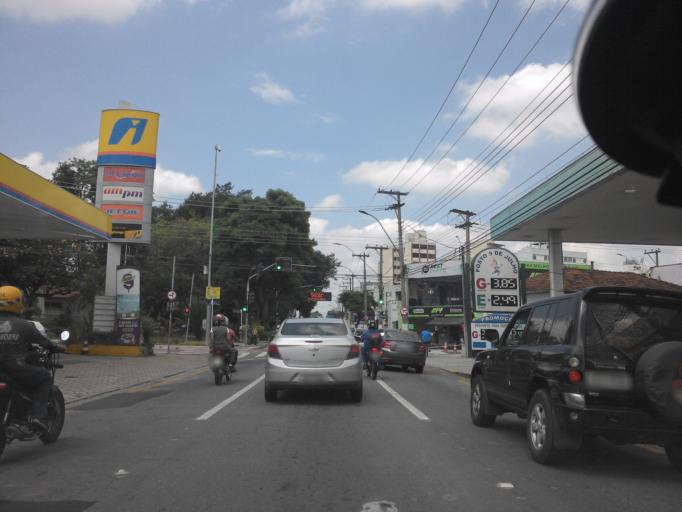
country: BR
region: Sao Paulo
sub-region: Taubate
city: Taubate
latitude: -23.0240
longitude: -45.5612
